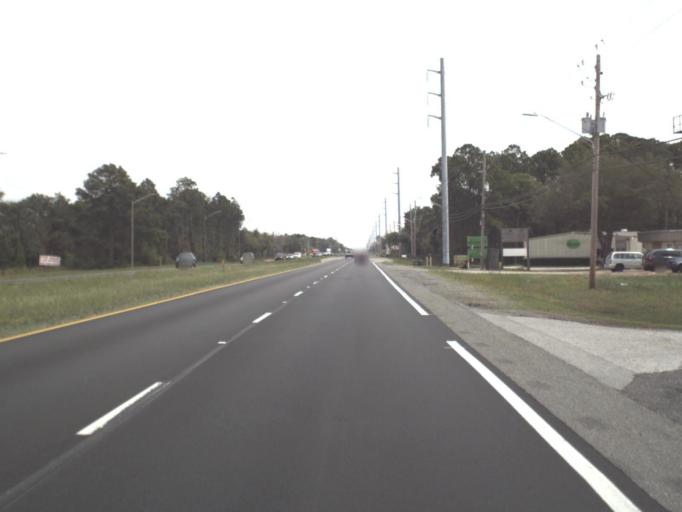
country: US
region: Florida
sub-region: Santa Rosa County
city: Tiger Point
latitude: 30.3939
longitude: -87.0386
